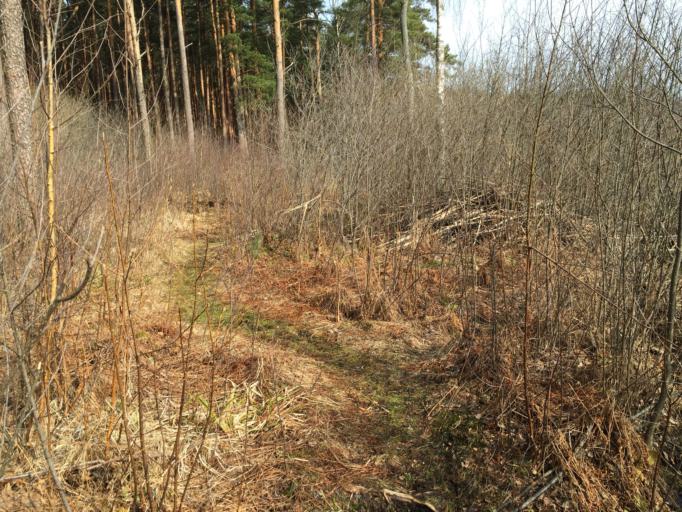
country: LV
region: Kekava
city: Balozi
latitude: 56.8752
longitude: 24.1324
